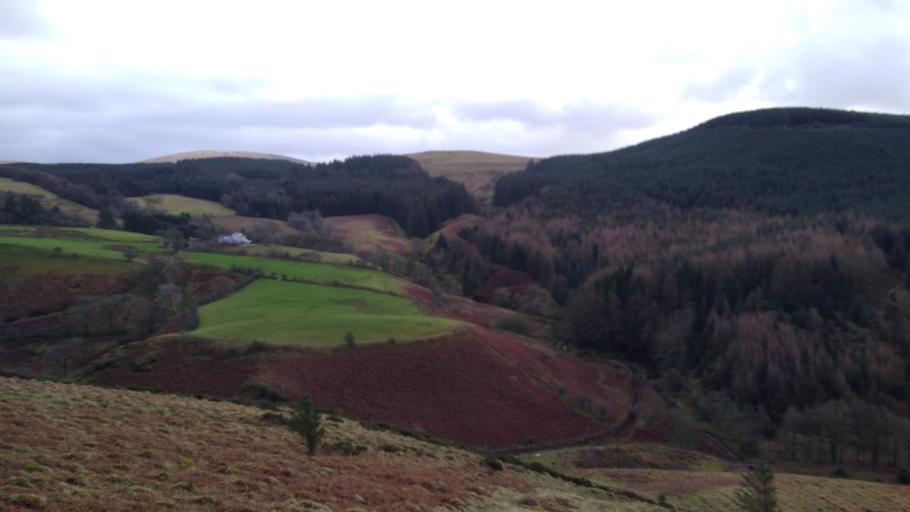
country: GB
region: England
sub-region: Cumbria
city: Frizington
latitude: 54.5012
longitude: -3.4659
